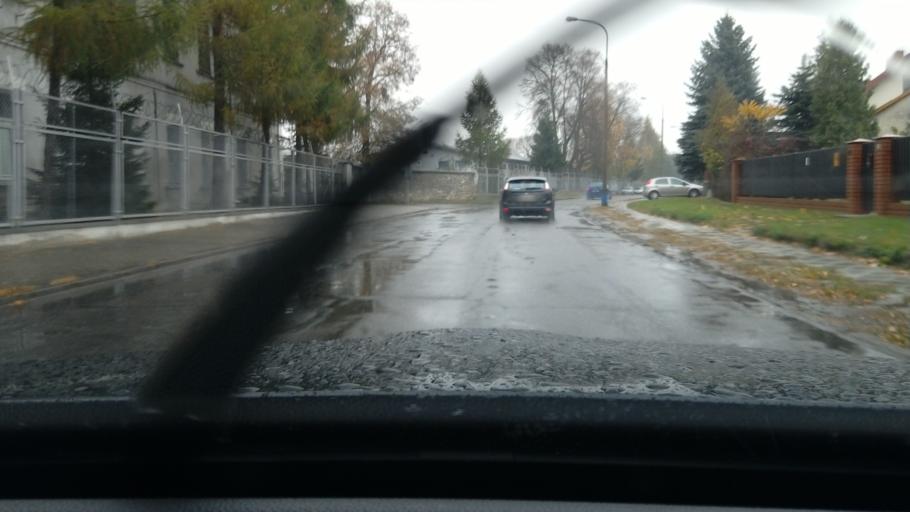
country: PL
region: Lodz Voivodeship
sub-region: Skierniewice
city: Skierniewice
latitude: 51.9473
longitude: 20.1466
